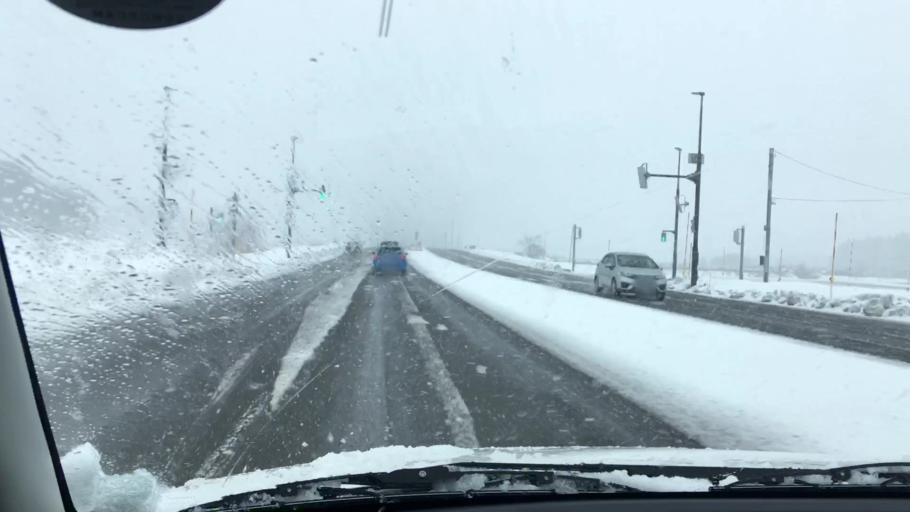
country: JP
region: Niigata
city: Joetsu
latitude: 37.0818
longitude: 138.2342
